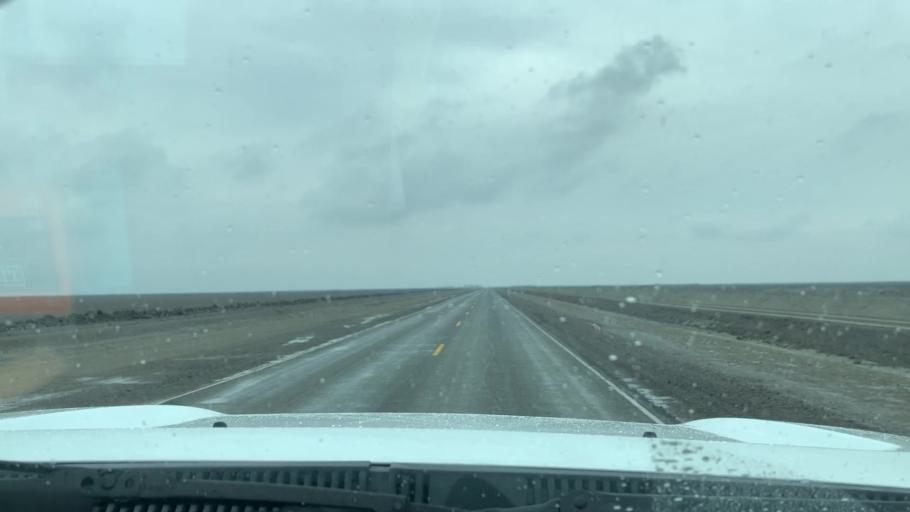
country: US
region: California
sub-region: Tulare County
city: Alpaugh
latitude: 35.9342
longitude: -119.6006
